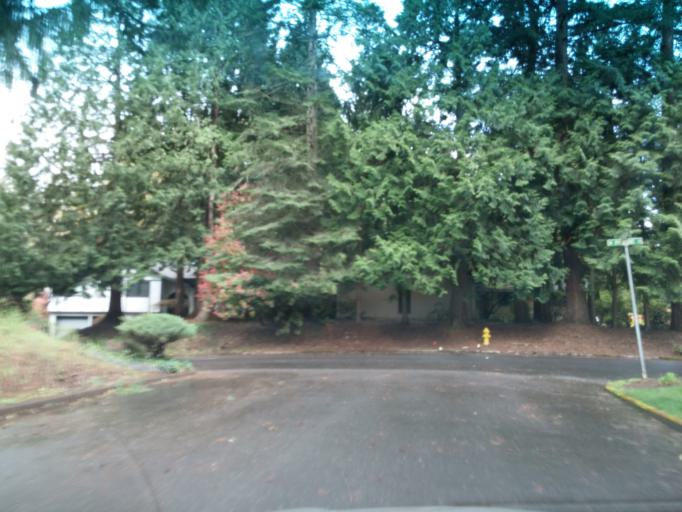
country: US
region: Oregon
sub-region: Washington County
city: Aloha
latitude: 45.5055
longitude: -122.8625
